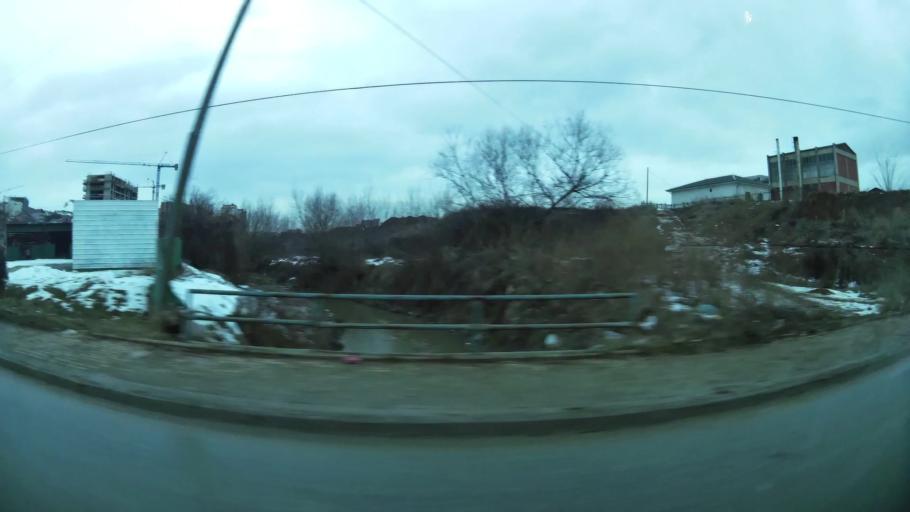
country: XK
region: Pristina
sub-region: Komuna e Prishtines
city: Pristina
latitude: 42.6412
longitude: 21.1639
